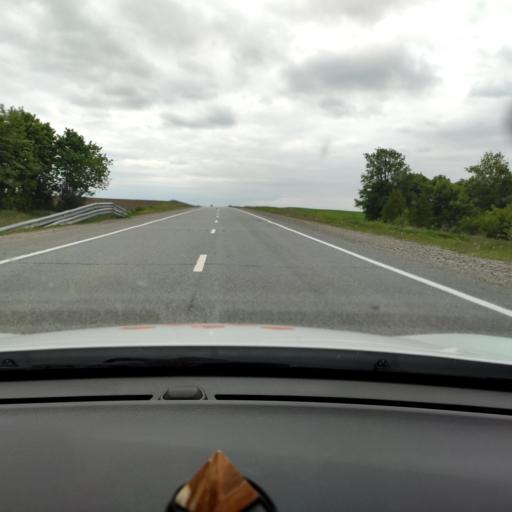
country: RU
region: Tatarstan
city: Pestretsy
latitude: 55.6341
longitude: 49.6892
